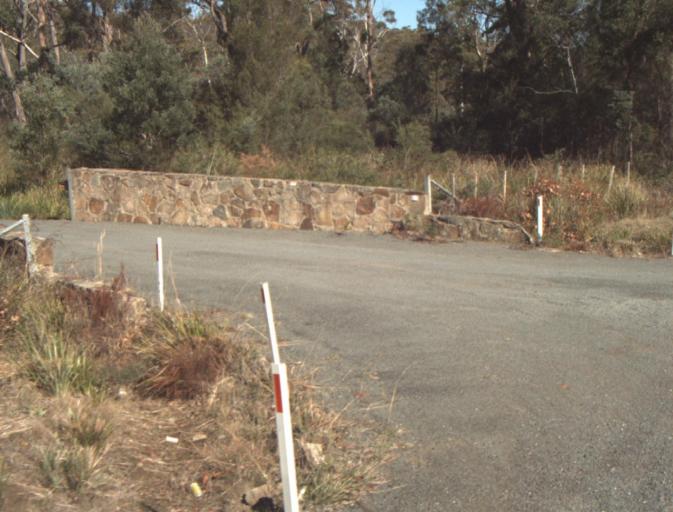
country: AU
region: Tasmania
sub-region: Launceston
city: Mayfield
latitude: -41.3403
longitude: 147.1437
